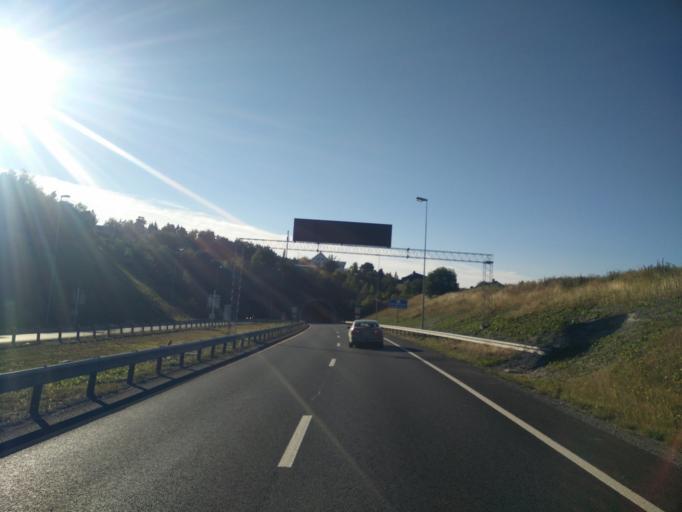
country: NO
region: Sor-Trondelag
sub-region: Trondheim
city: Trondheim
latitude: 63.4266
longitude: 10.5133
